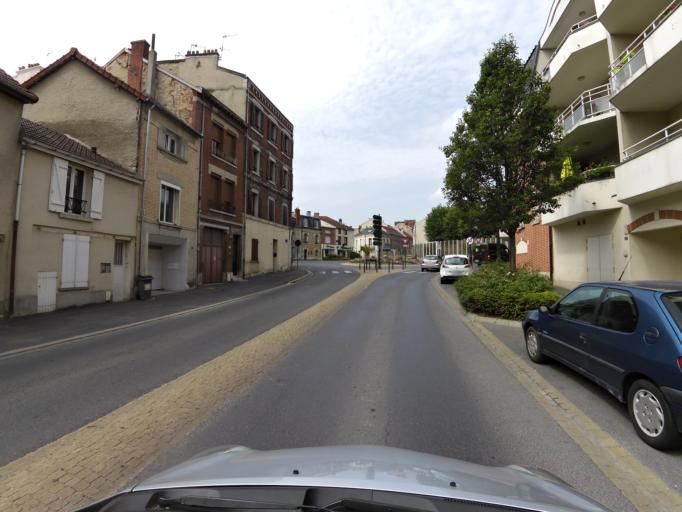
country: FR
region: Champagne-Ardenne
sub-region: Departement de la Marne
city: Epernay
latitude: 49.0463
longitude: 3.9519
